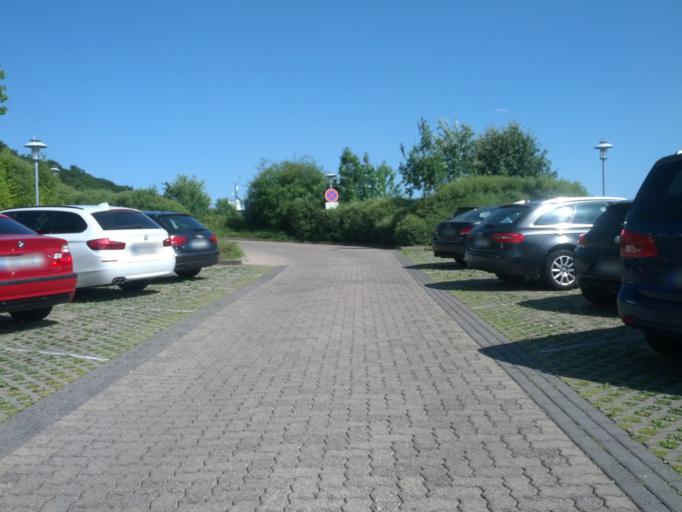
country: DE
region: Thuringia
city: Krauthausen
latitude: 50.9895
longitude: 10.2689
